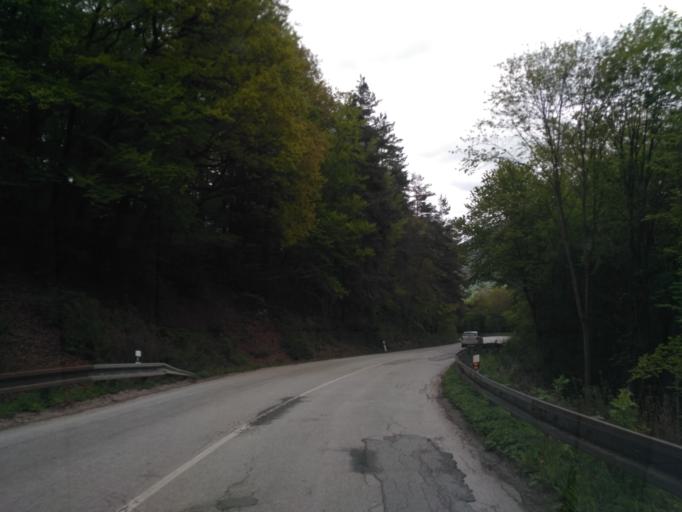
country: SK
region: Kosicky
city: Dobsina
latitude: 48.6427
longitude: 20.3574
